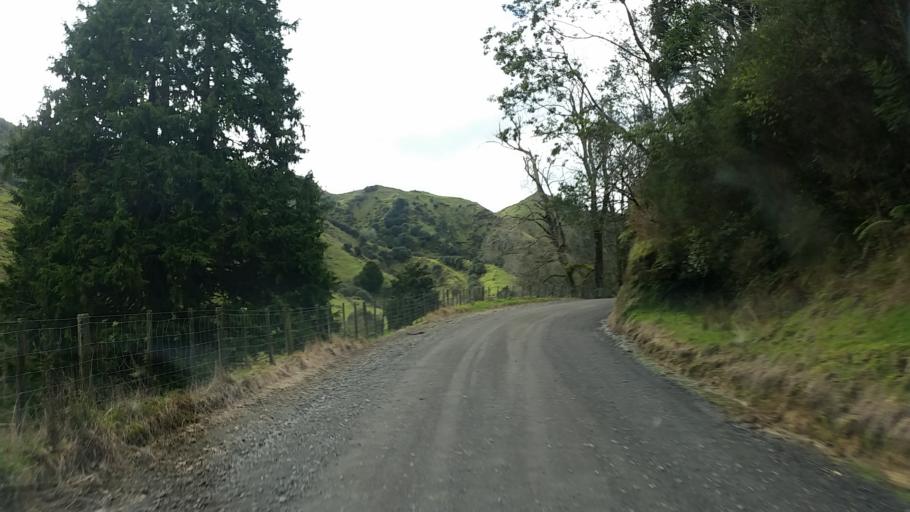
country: NZ
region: Taranaki
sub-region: New Plymouth District
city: Waitara
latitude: -39.1638
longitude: 174.5732
